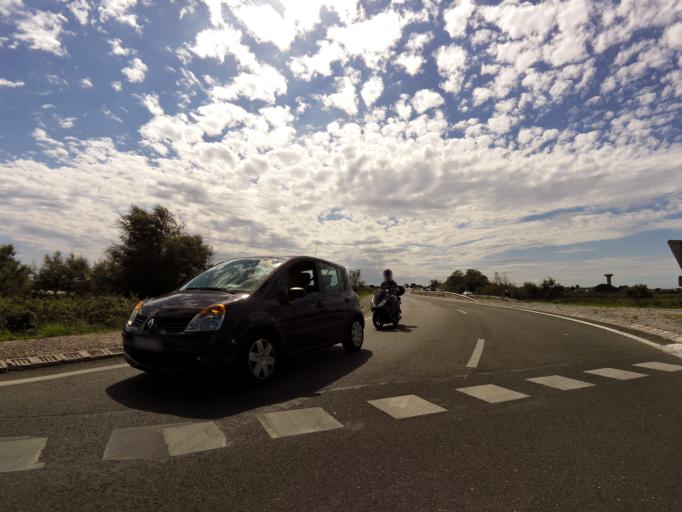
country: FR
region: Languedoc-Roussillon
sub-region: Departement du Gard
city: Le Grau-du-Roi
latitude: 43.5505
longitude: 4.1394
